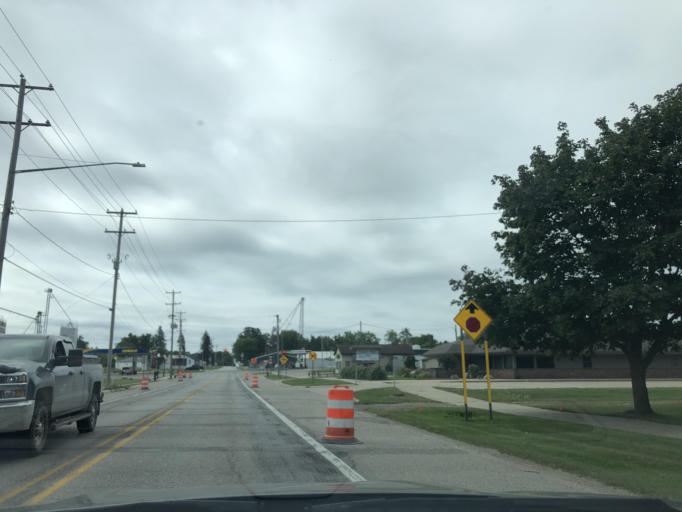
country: US
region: Michigan
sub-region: Missaukee County
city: Lake City
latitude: 44.1953
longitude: -85.2138
